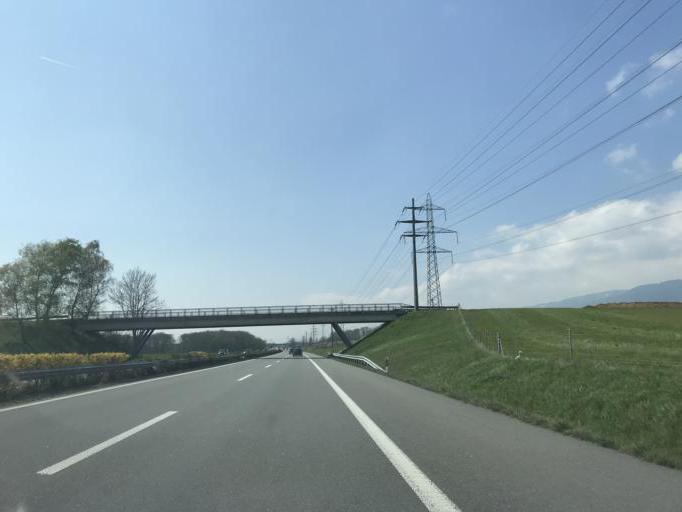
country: CH
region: Vaud
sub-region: Nyon District
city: Gland
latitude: 46.4366
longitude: 6.2773
